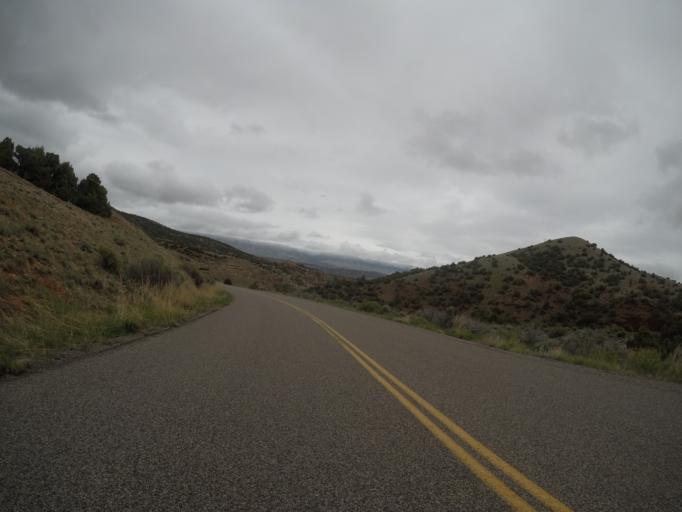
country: US
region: Wyoming
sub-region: Big Horn County
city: Lovell
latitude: 45.1084
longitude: -108.2415
